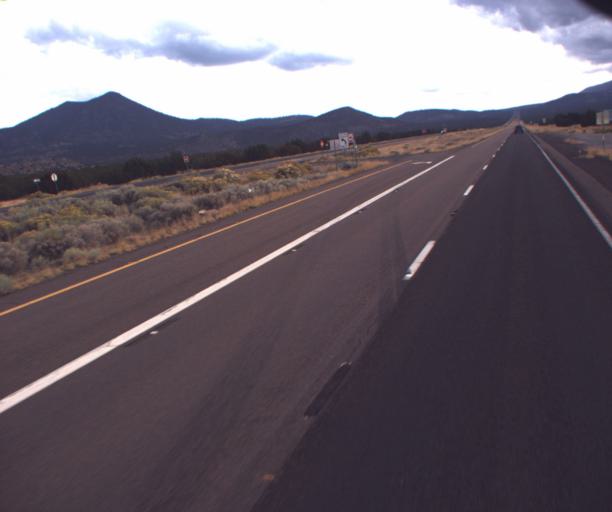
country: US
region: Arizona
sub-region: Coconino County
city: Flagstaff
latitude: 35.4557
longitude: -111.5620
